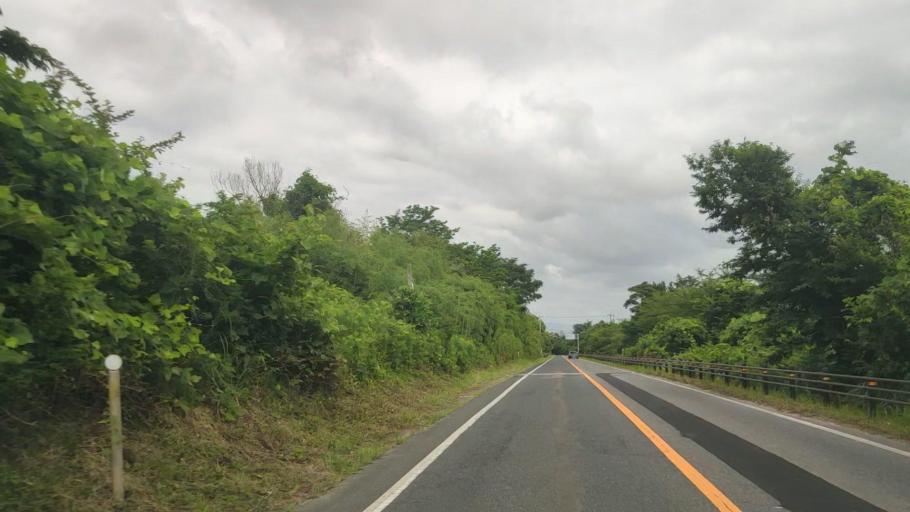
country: JP
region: Tottori
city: Yonago
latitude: 35.4217
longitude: 133.4304
